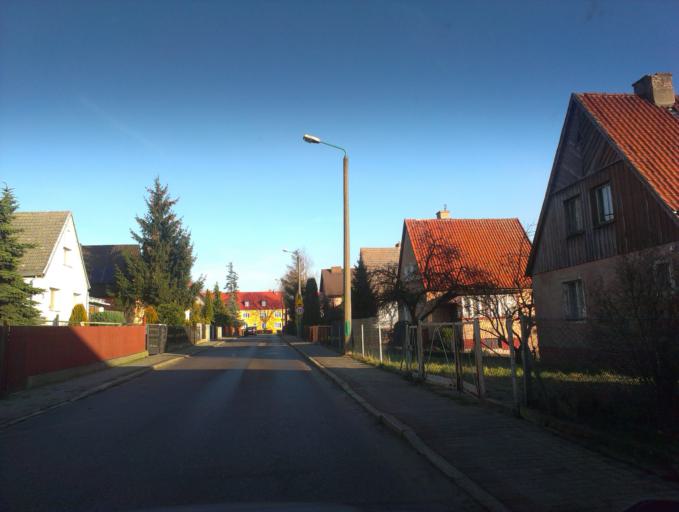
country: PL
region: West Pomeranian Voivodeship
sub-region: Powiat szczecinecki
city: Szczecinek
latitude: 53.7007
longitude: 16.7053
